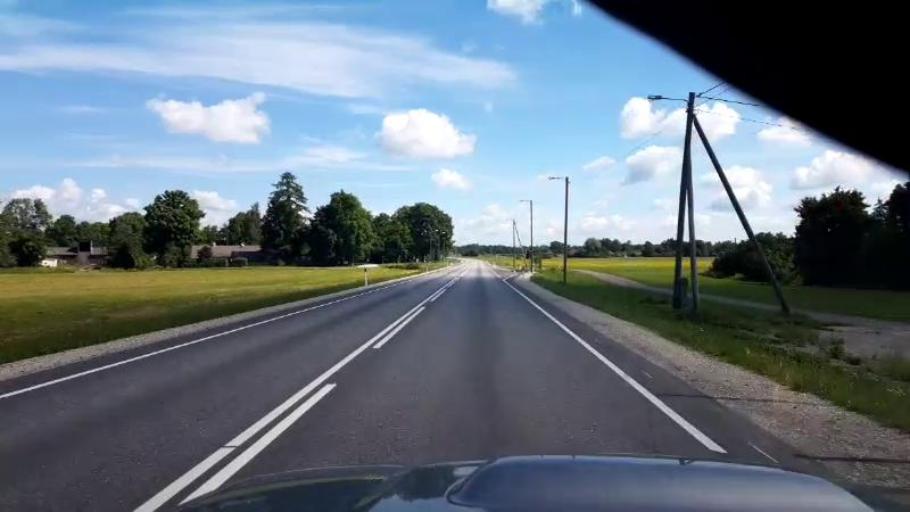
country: EE
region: Jaervamaa
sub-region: Jaerva-Jaani vald
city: Jarva-Jaani
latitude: 59.1111
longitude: 25.7258
